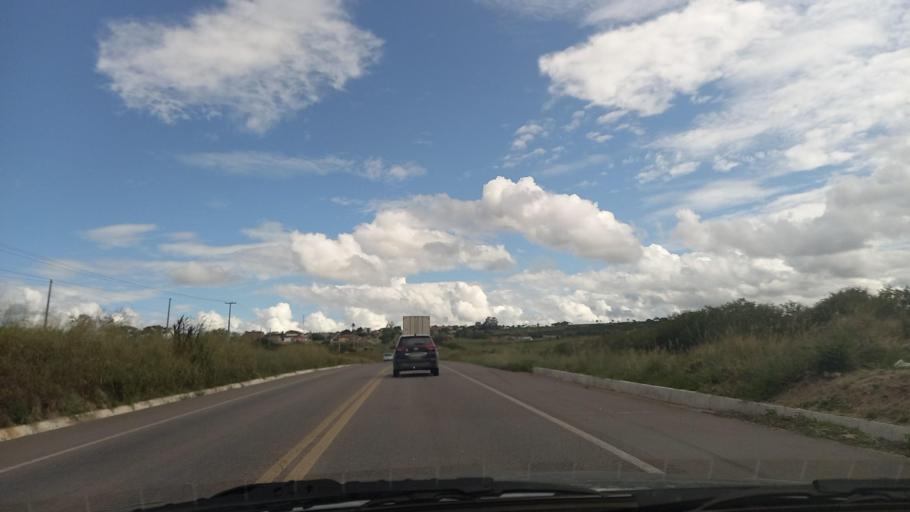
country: BR
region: Pernambuco
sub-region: Lajedo
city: Lajedo
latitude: -8.6993
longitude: -36.4147
